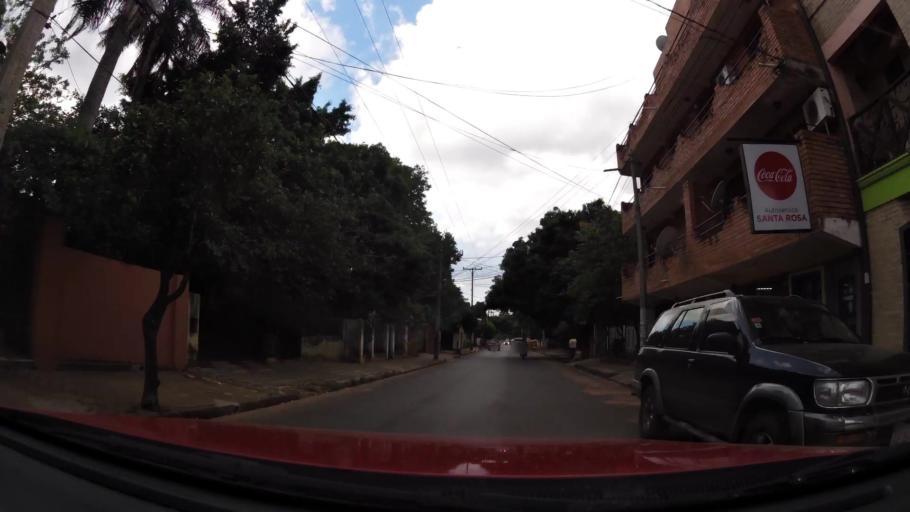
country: PY
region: Central
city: Fernando de la Mora
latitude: -25.3358
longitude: -57.5443
